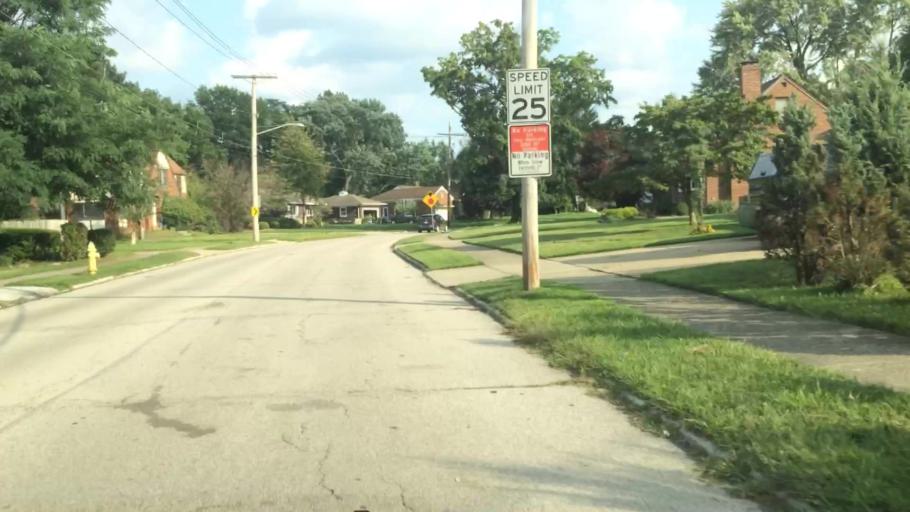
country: US
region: Ohio
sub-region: Cuyahoga County
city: Parma Heights
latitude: 41.4027
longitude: -81.7452
